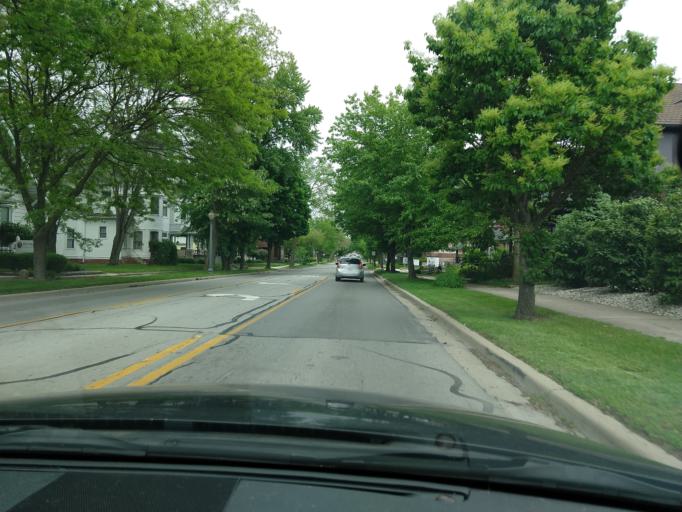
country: US
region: Indiana
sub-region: Hamilton County
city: Noblesville
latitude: 40.0455
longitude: -86.0107
